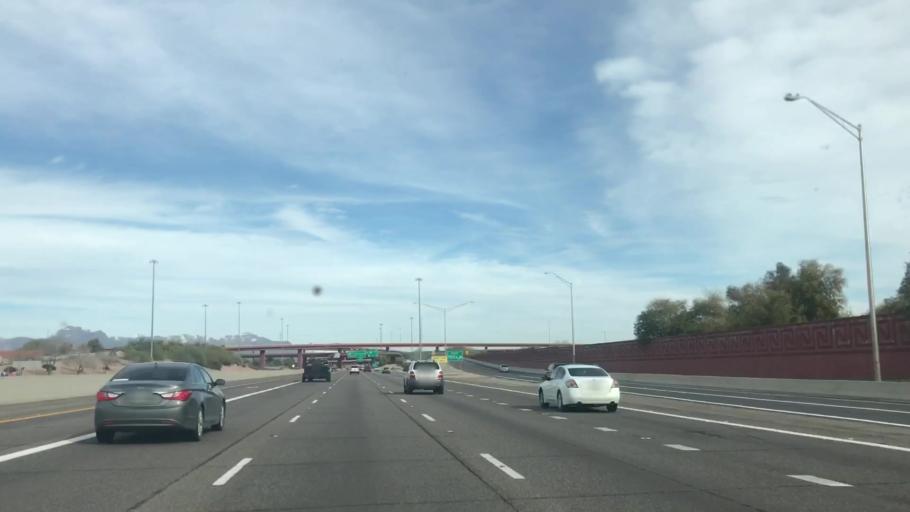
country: US
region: Arizona
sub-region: Pinal County
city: Apache Junction
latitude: 33.3864
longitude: -111.6576
